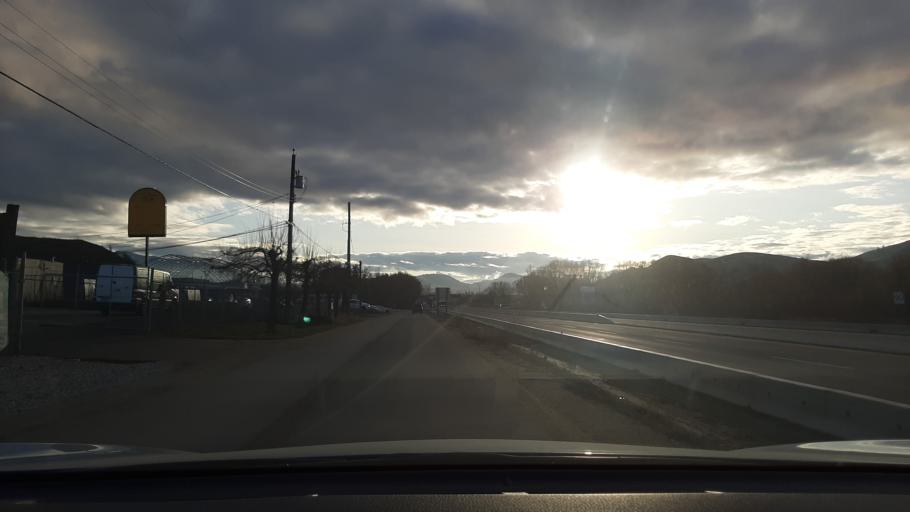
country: CA
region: British Columbia
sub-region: Regional District of North Okanagan
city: Vernon
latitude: 50.2950
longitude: -119.2561
